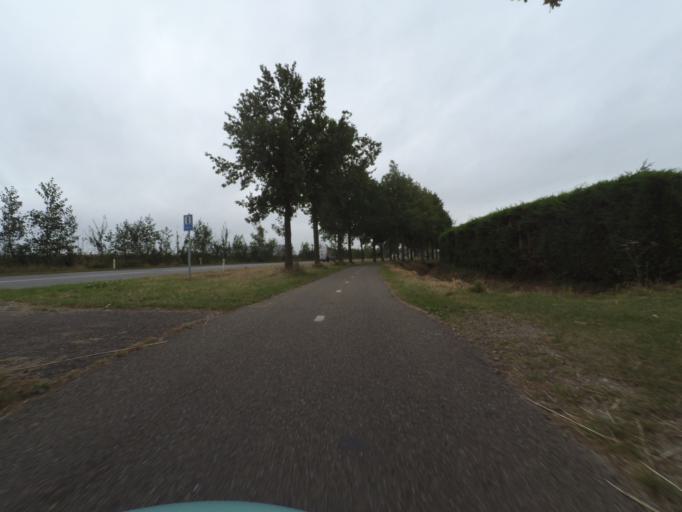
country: NL
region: Gelderland
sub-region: Gemeente Geldermalsen
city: Geldermalsen
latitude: 51.9198
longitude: 5.3288
